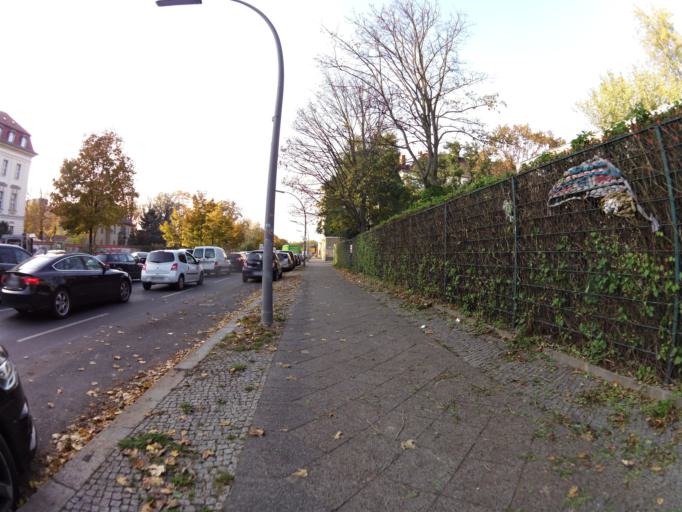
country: DE
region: Berlin
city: Wedding Bezirk
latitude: 52.5445
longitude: 13.3466
